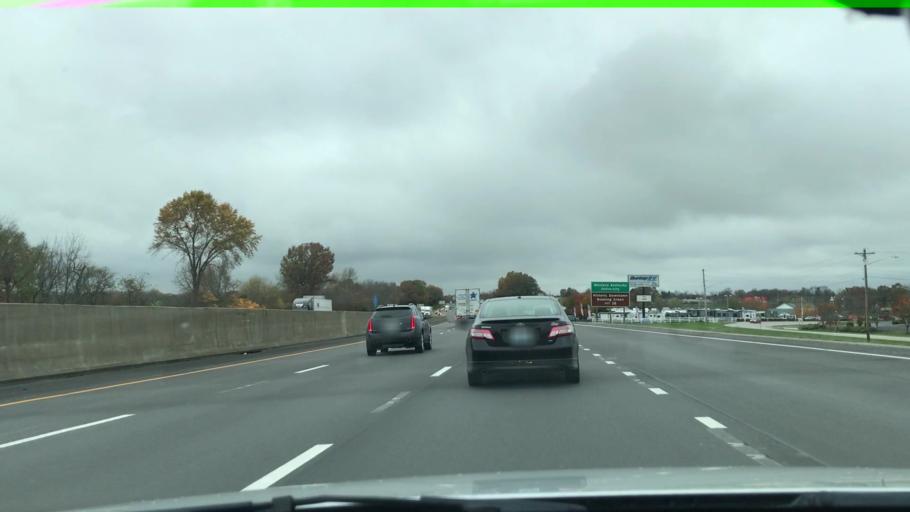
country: US
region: Kentucky
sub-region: Warren County
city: Bowling Green
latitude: 37.0040
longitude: -86.3717
